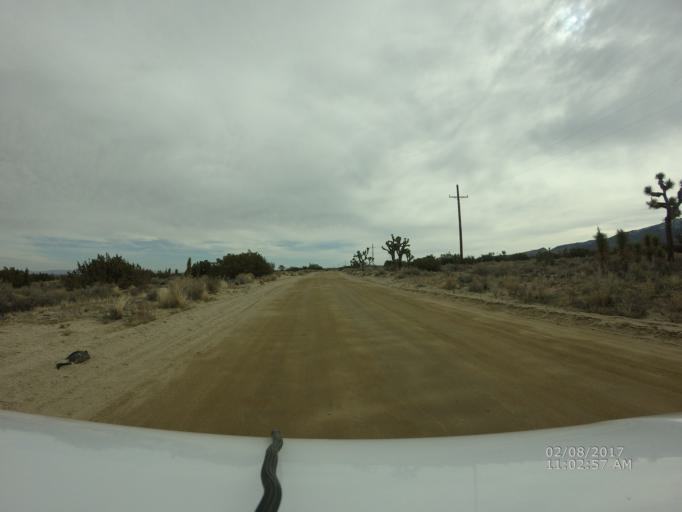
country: US
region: California
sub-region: San Bernardino County
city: Pinon Hills
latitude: 34.4569
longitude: -117.6753
